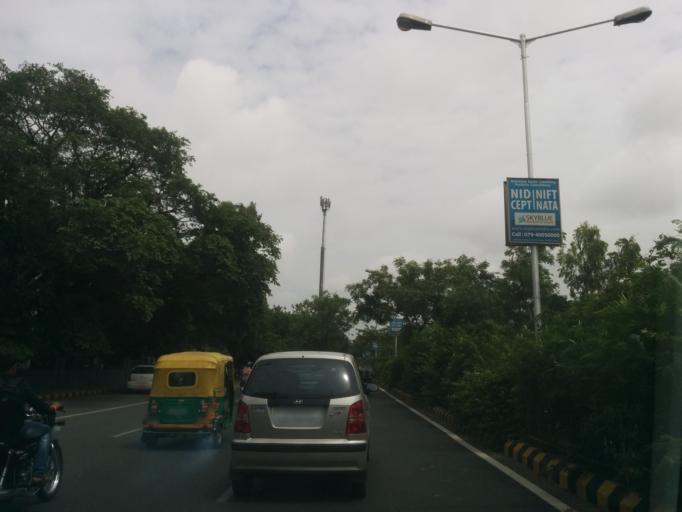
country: IN
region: Gujarat
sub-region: Ahmadabad
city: Ahmedabad
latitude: 23.0364
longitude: 72.5486
